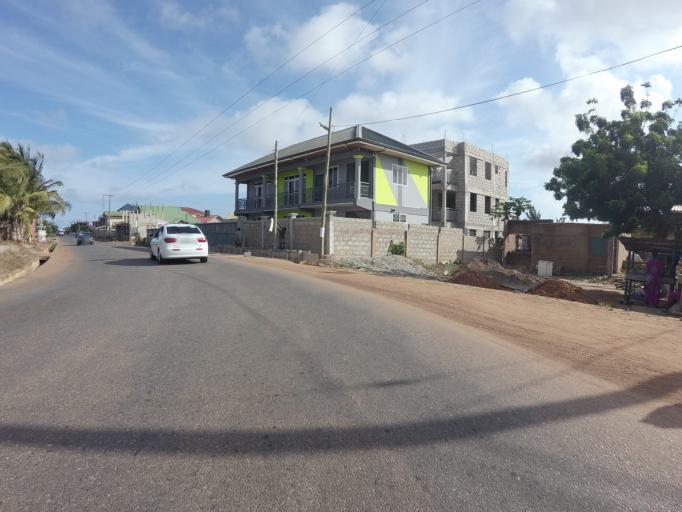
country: GH
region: Greater Accra
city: Teshi Old Town
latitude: 5.5819
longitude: -0.1426
